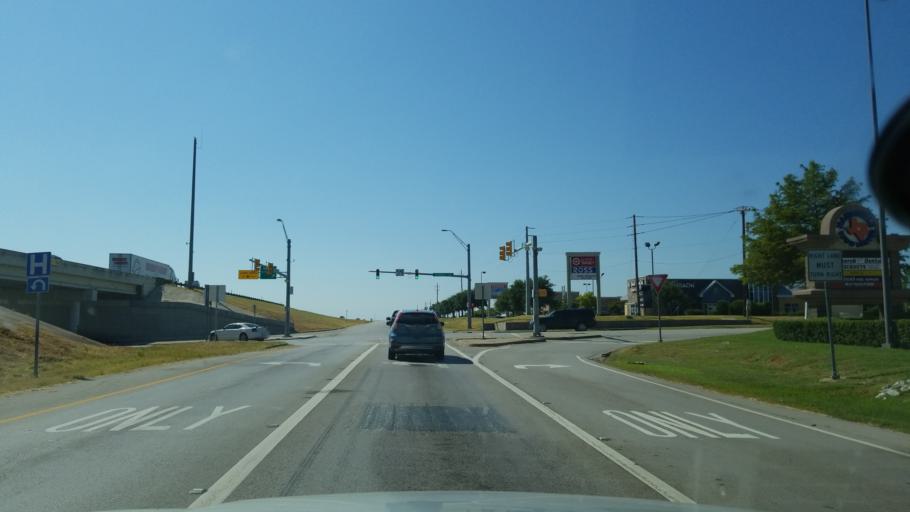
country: US
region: Texas
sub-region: Tarrant County
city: Mansfield
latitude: 32.5932
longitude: -97.1446
